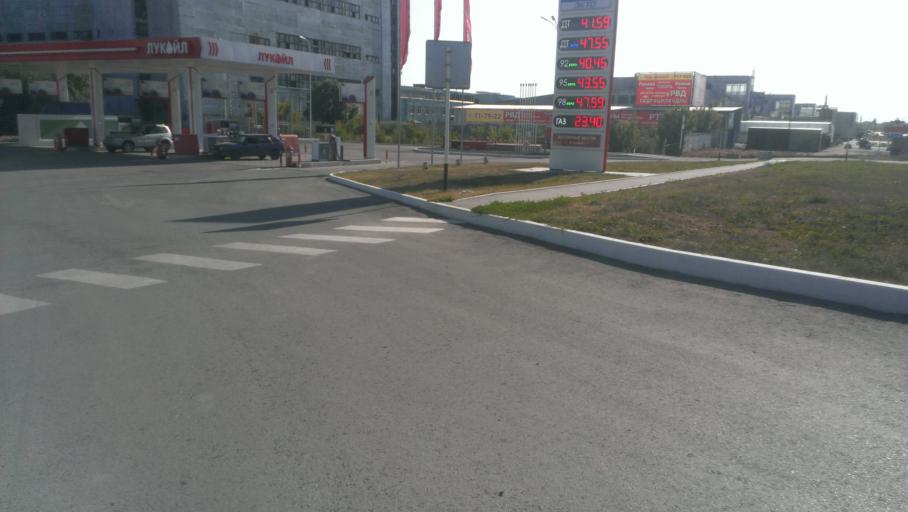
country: RU
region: Altai Krai
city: Novosilikatnyy
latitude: 53.3240
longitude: 83.6451
